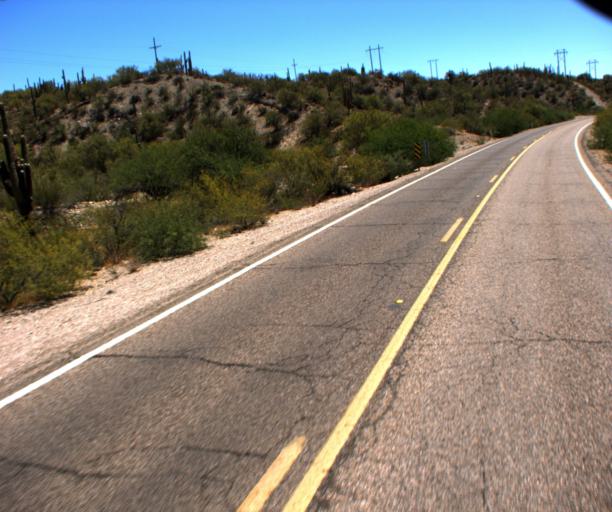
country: US
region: Arizona
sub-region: Pinal County
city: Kearny
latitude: 33.0143
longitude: -110.8295
